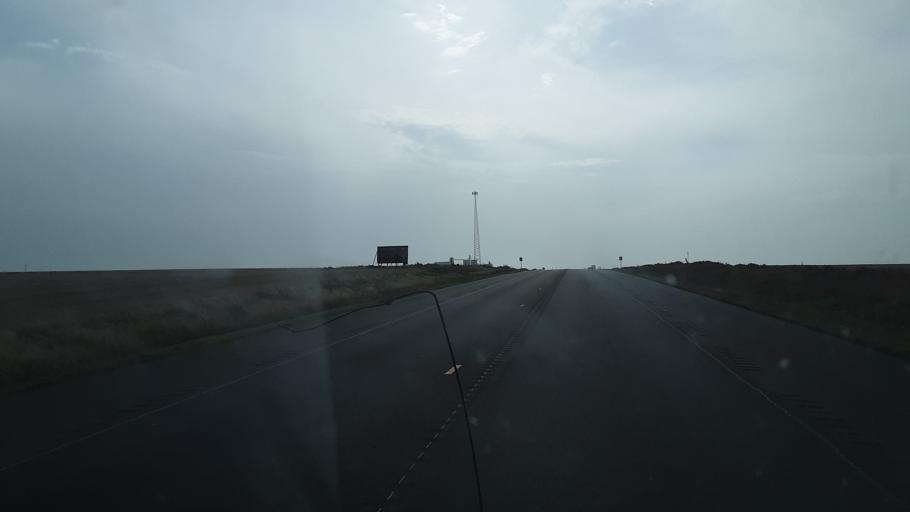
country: US
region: Kansas
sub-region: Ford County
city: Dodge City
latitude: 37.7788
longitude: -99.9166
